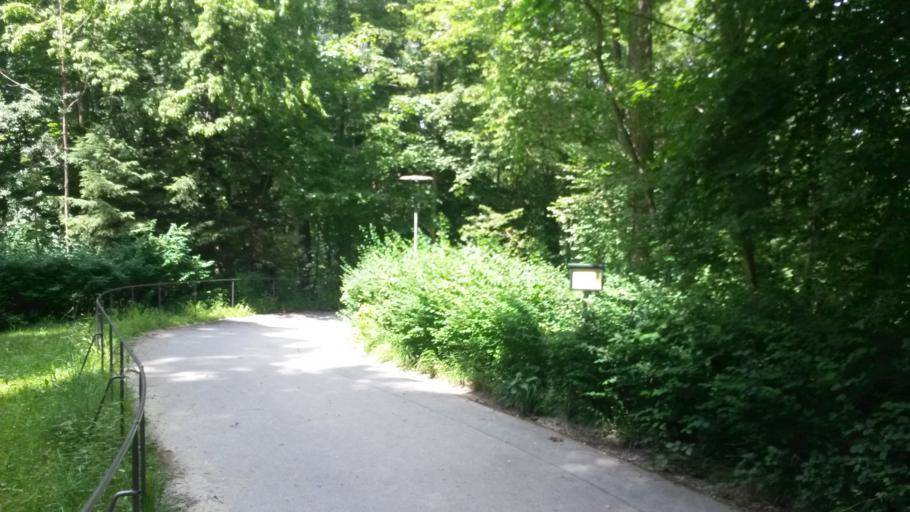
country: DE
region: Bavaria
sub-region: Upper Bavaria
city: Chiemsee
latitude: 47.8613
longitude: 12.4013
